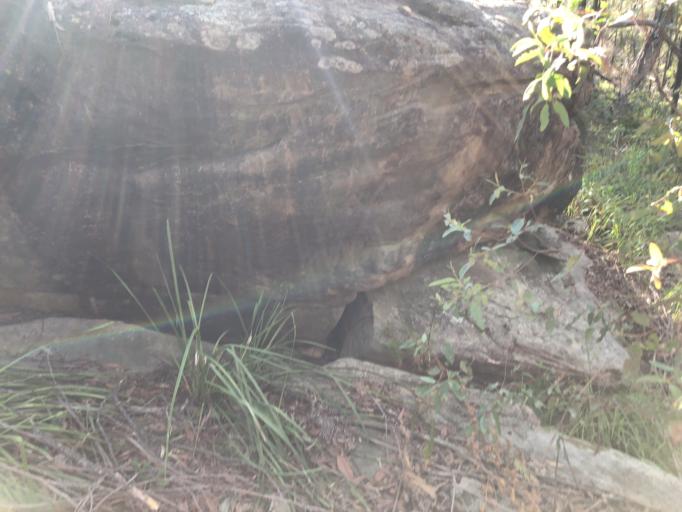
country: AU
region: New South Wales
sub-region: Hawkesbury
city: Scheyville
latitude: -33.5669
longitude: 150.9317
